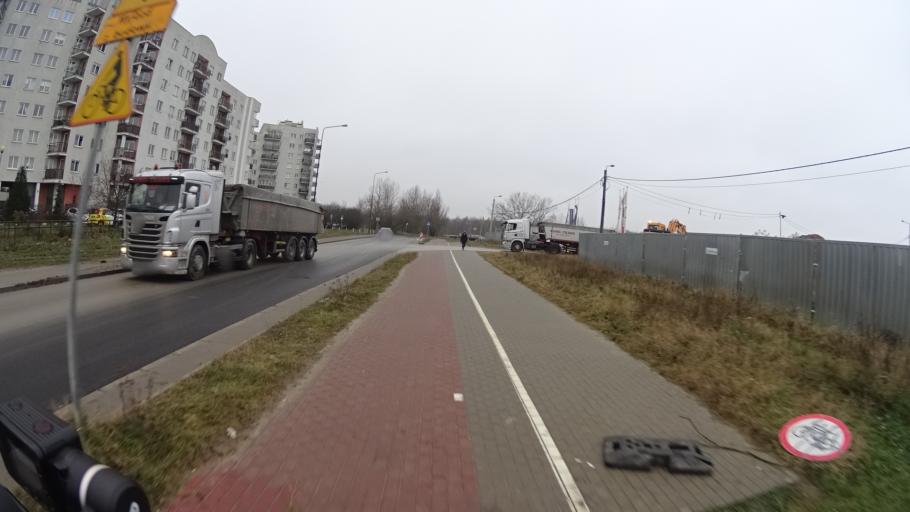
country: PL
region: Masovian Voivodeship
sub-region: Warszawa
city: Ursynow
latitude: 52.1396
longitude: 21.0388
